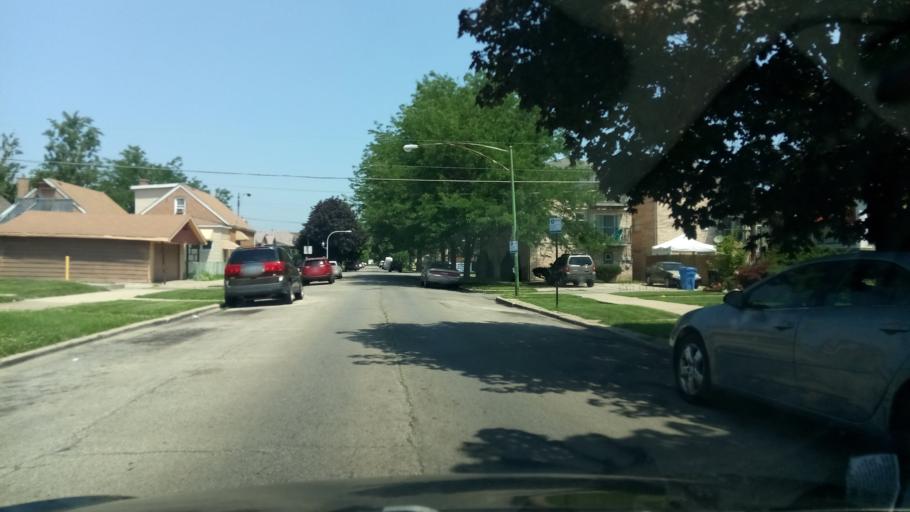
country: US
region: Illinois
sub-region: Cook County
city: Hometown
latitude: 41.7848
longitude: -87.7289
